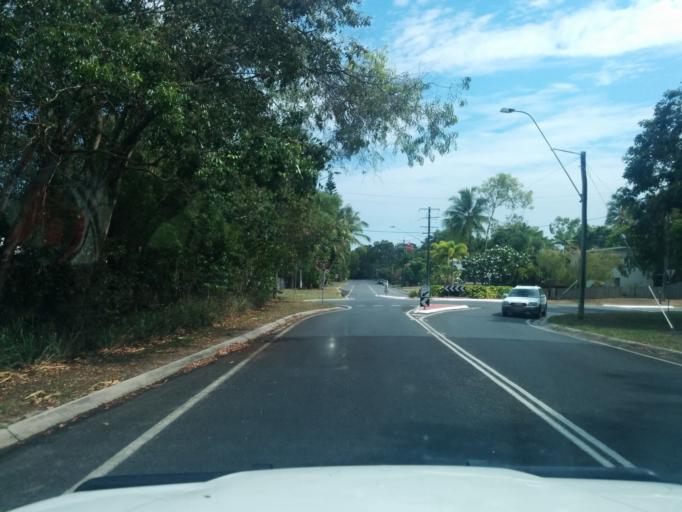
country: AU
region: Queensland
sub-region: Cairns
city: Yorkeys Knob
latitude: -16.8425
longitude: 145.7354
